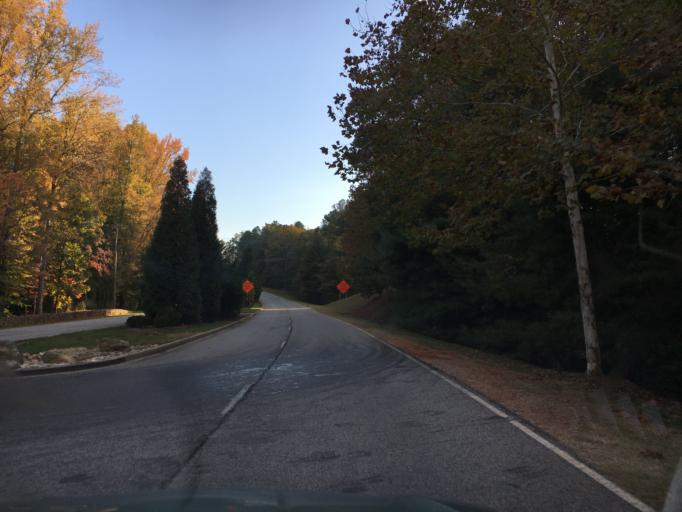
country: US
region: South Carolina
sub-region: Greenville County
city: Greer
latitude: 34.8857
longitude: -82.2155
